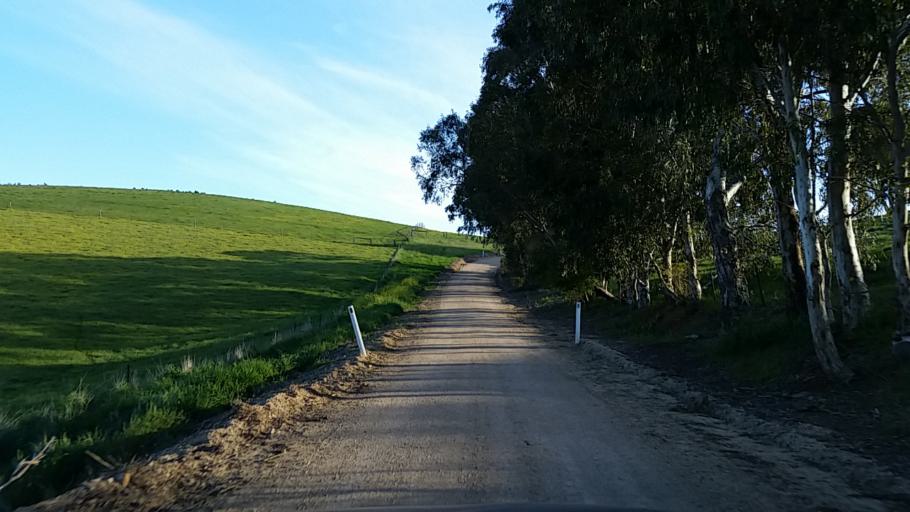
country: AU
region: South Australia
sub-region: Mount Barker
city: Meadows
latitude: -35.2411
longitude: 138.7615
